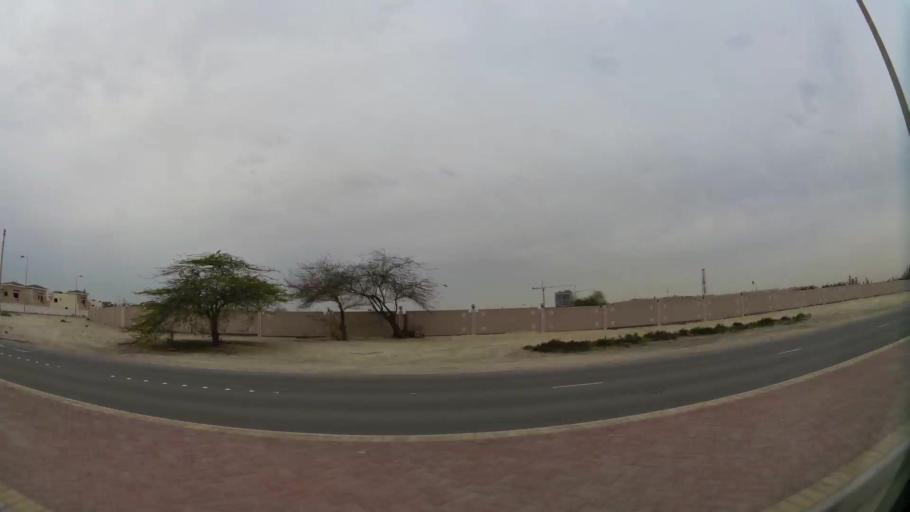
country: BH
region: Northern
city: Ar Rifa'
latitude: 26.0958
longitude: 50.5577
